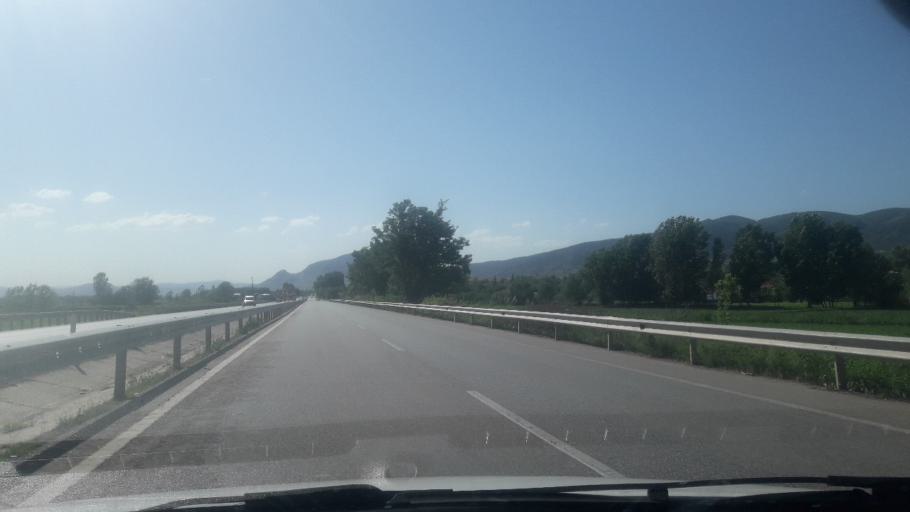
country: TR
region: Tokat
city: Dokmetepe
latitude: 40.3085
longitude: 36.2962
